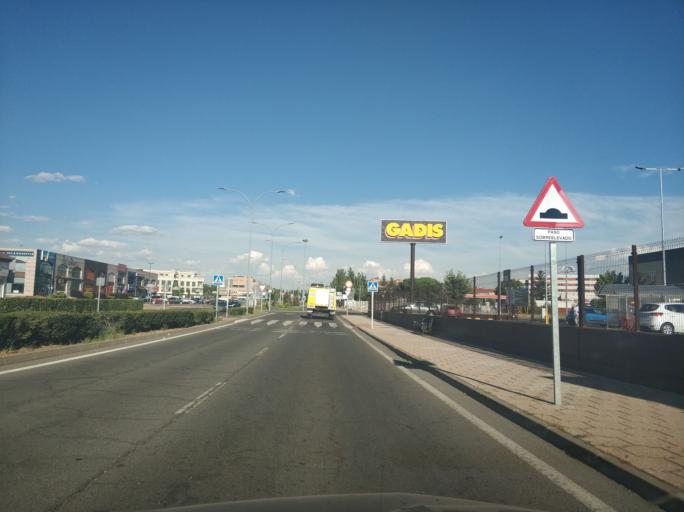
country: ES
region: Castille and Leon
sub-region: Provincia de Salamanca
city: Santa Marta de Tormes
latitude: 40.9509
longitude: -5.6429
